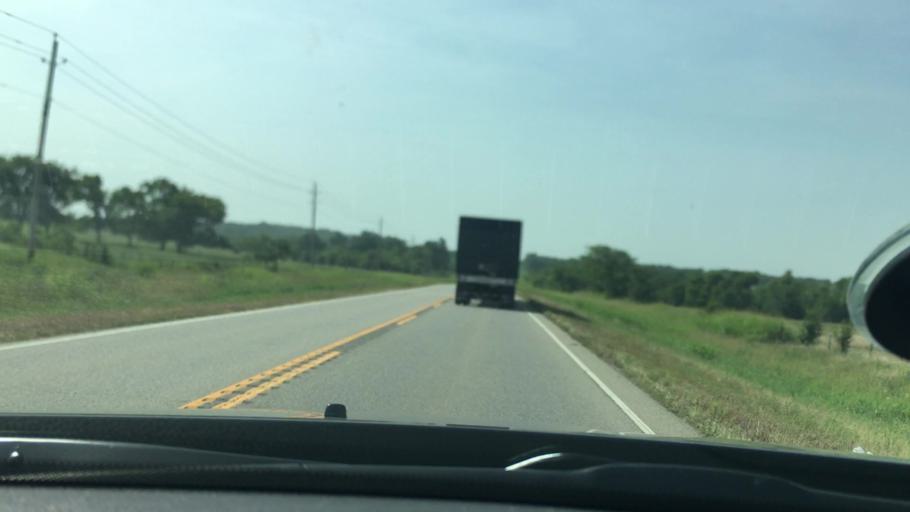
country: US
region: Oklahoma
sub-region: Coal County
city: Coalgate
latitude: 34.4560
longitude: -96.2128
